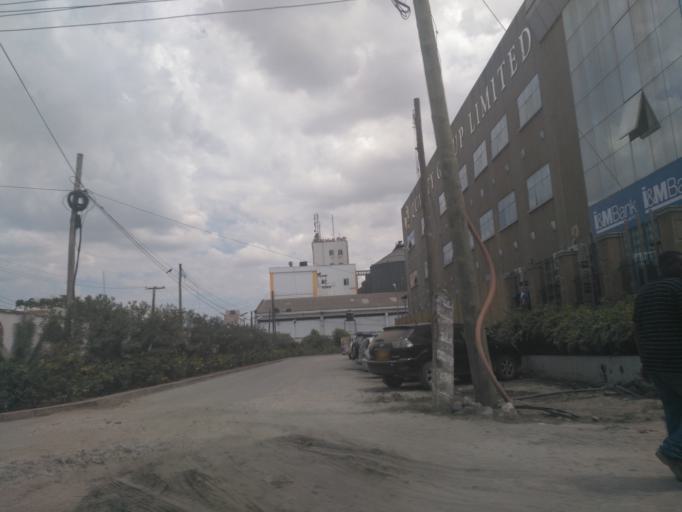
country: TZ
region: Dar es Salaam
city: Dar es Salaam
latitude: -6.8347
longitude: 39.2652
